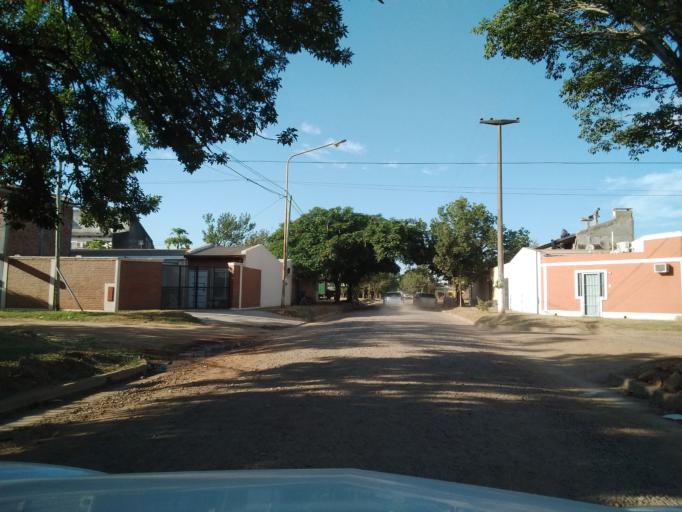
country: AR
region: Corrientes
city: Corrientes
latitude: -27.4910
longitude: -58.7832
